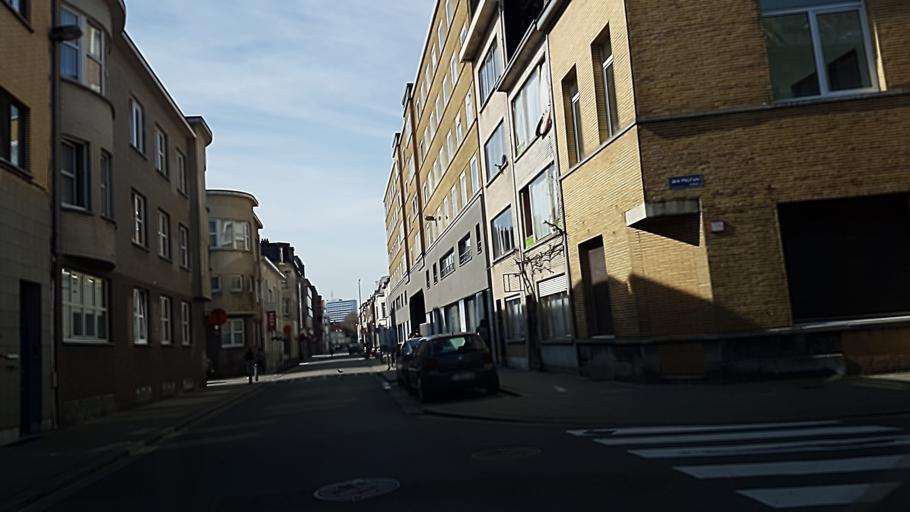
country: BE
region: Flanders
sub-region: Provincie Antwerpen
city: Antwerpen
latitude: 51.2225
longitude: 4.4311
